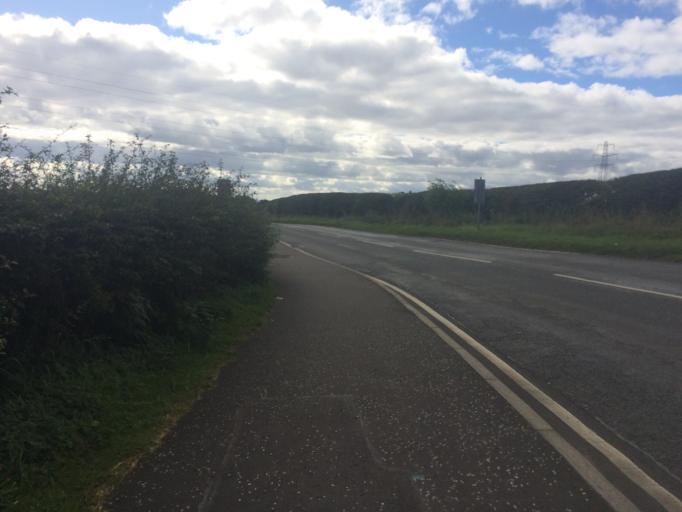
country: GB
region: Scotland
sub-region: Fife
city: Townhill
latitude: 56.0946
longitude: -3.4132
